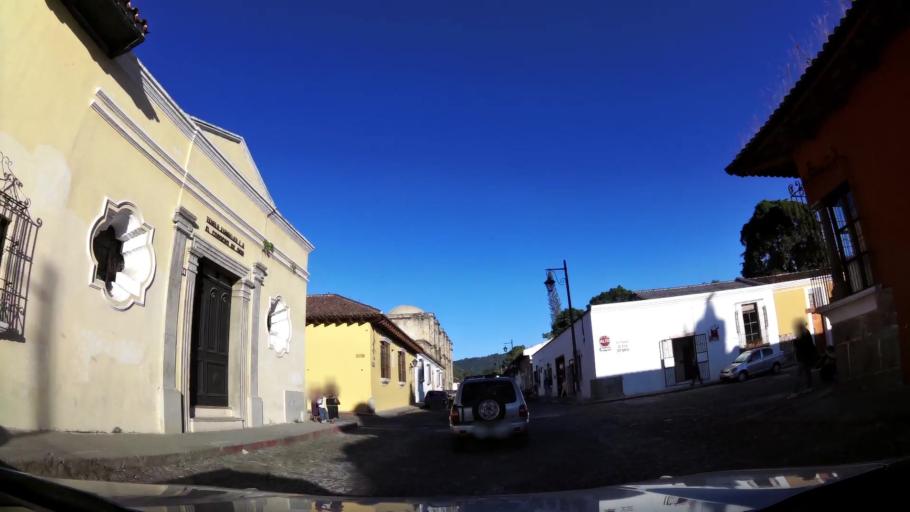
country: GT
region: Sacatepequez
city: Antigua Guatemala
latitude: 14.5593
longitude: -90.7323
